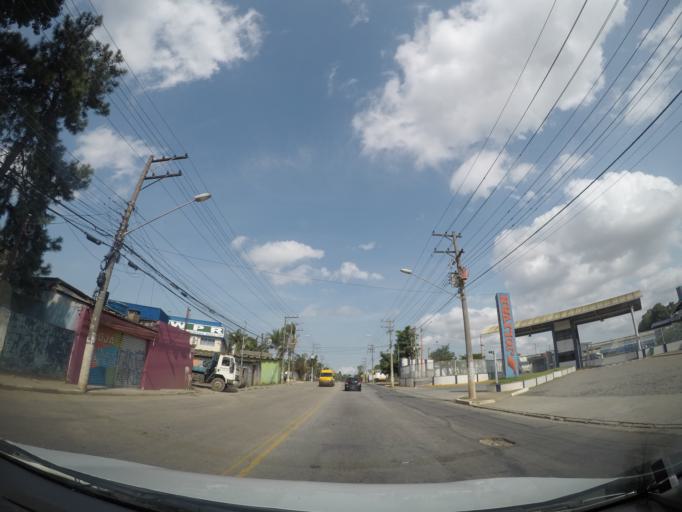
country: BR
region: Sao Paulo
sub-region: Guarulhos
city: Guarulhos
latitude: -23.4350
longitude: -46.4493
